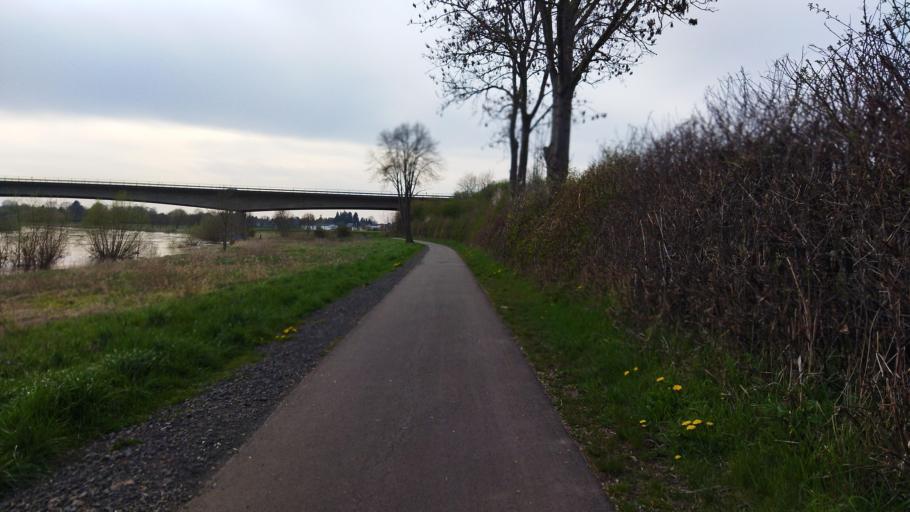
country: DE
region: Lower Saxony
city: Rinteln
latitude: 52.1949
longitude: 9.0978
